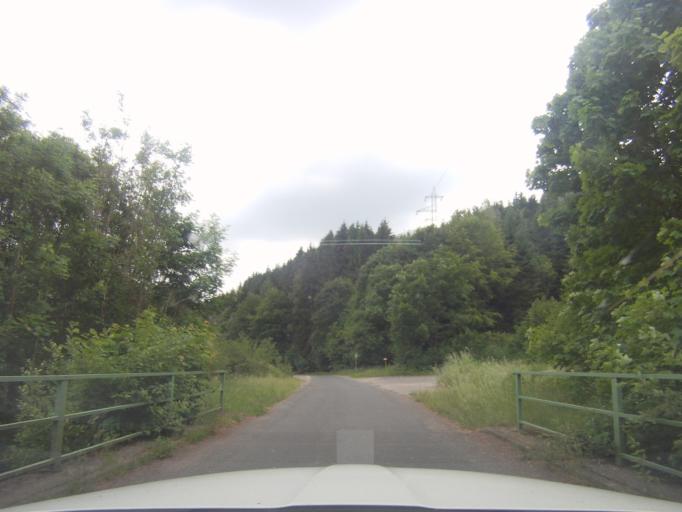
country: DE
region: Thuringia
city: Frauenwald
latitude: 50.5277
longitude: 10.8798
